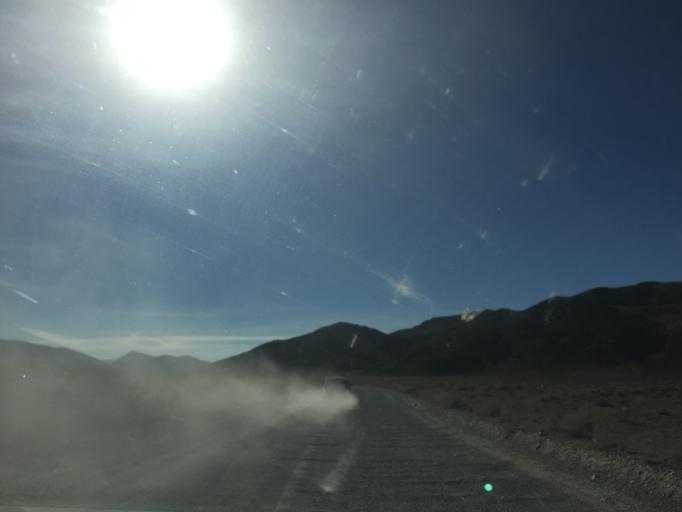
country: US
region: California
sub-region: Inyo County
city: Lone Pine
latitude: 36.8292
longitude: -117.5067
